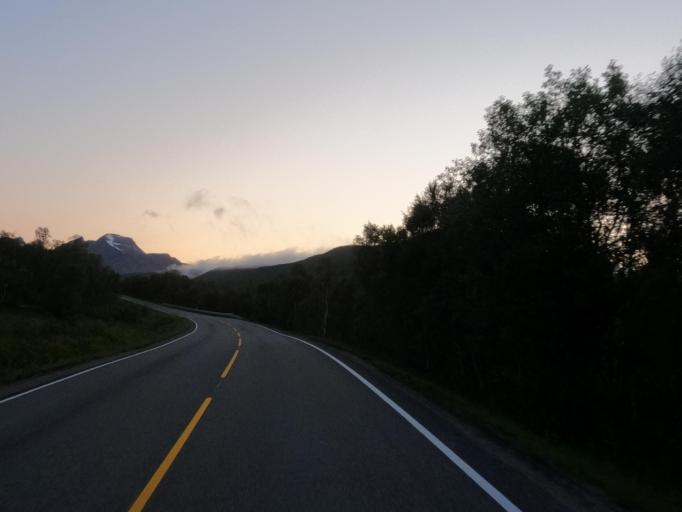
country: NO
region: Nordland
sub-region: Lodingen
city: Lodingen
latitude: 68.5218
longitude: 15.8572
